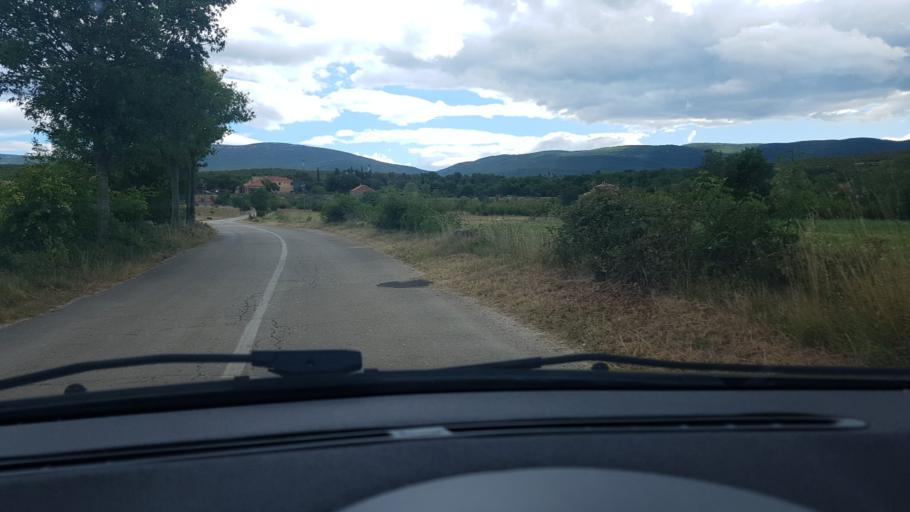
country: HR
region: Zadarska
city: Gracac
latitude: 44.1602
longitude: 15.8577
